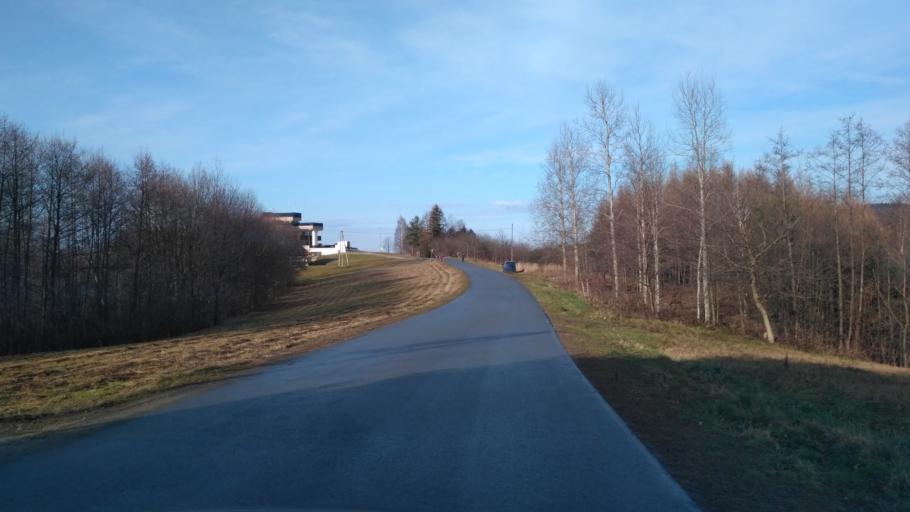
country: PL
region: Subcarpathian Voivodeship
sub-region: Powiat krosnienski
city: Korczyna
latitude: 49.7311
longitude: 21.7877
